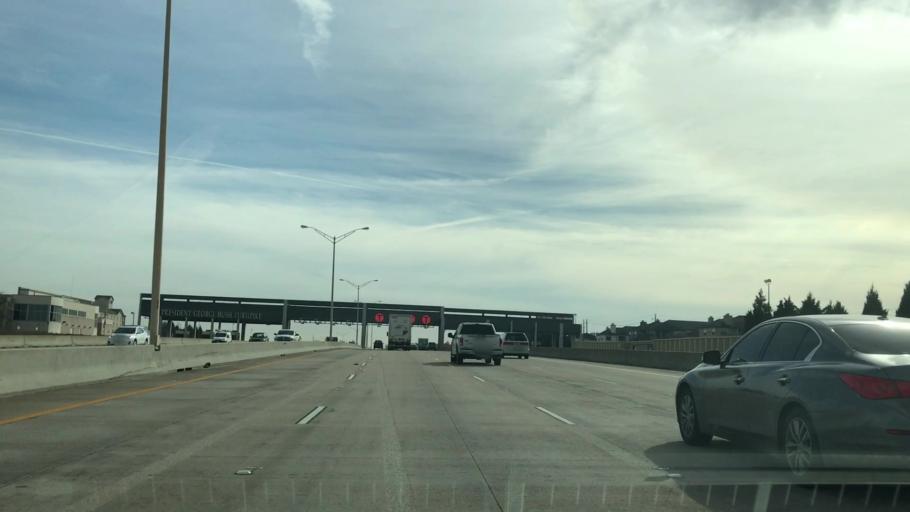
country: US
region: Texas
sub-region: Dallas County
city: Addison
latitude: 33.0033
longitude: -96.7784
